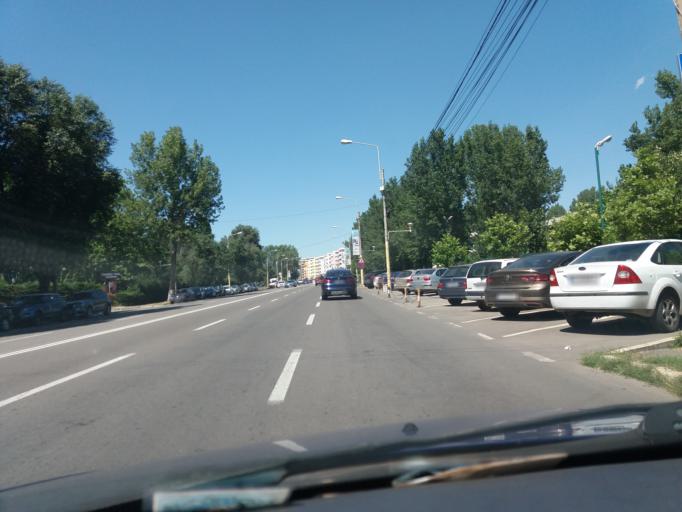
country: RO
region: Constanta
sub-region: Municipiul Constanta
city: Palazu Mare
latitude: 44.2625
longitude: 28.6183
